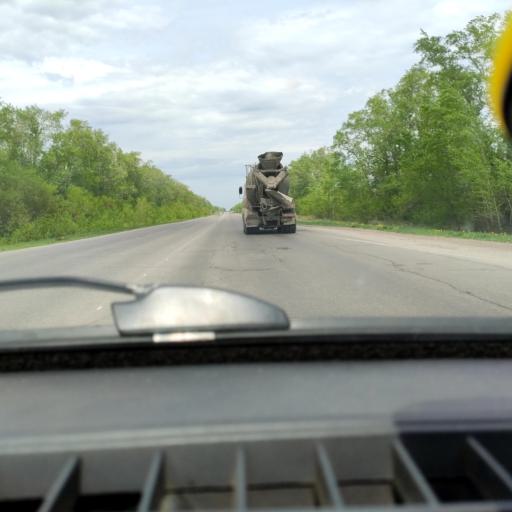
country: RU
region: Samara
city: Tol'yatti
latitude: 53.5979
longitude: 49.4083
